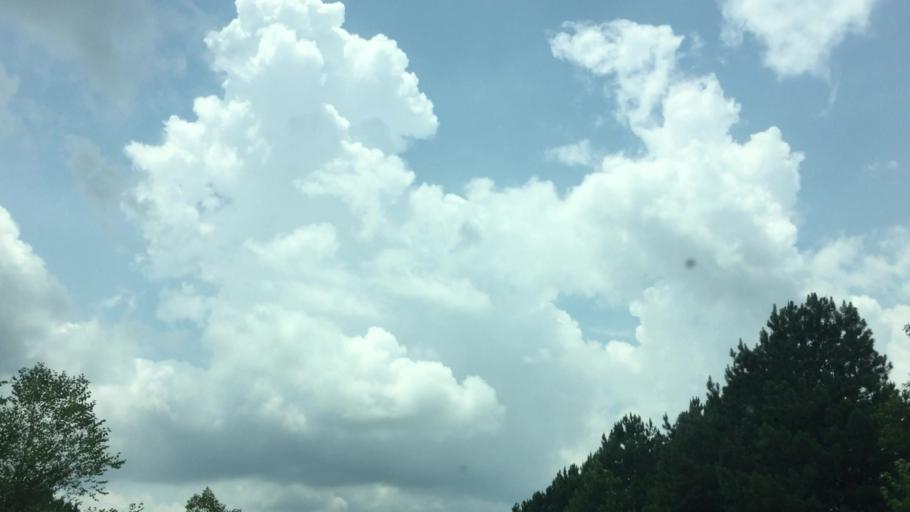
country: US
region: Georgia
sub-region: Fulton County
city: Fairburn
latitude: 33.6230
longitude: -84.5912
